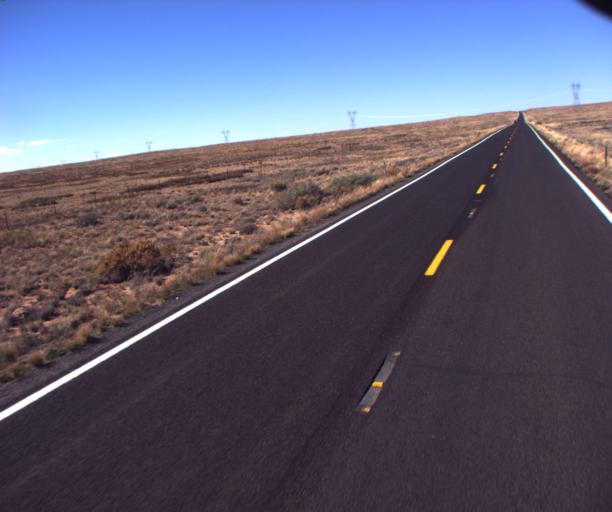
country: US
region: Arizona
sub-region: Coconino County
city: Tuba City
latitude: 35.9470
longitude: -110.9168
